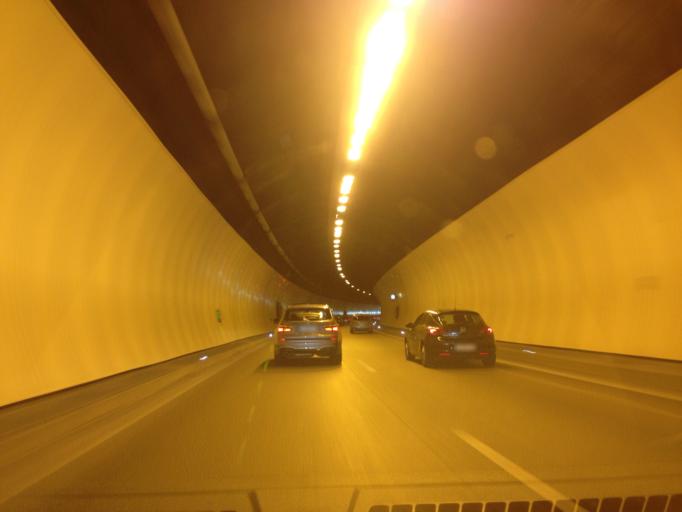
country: DE
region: Baden-Wuerttemberg
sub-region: Tuebingen Region
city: Ulm
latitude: 48.4127
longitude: 9.9726
